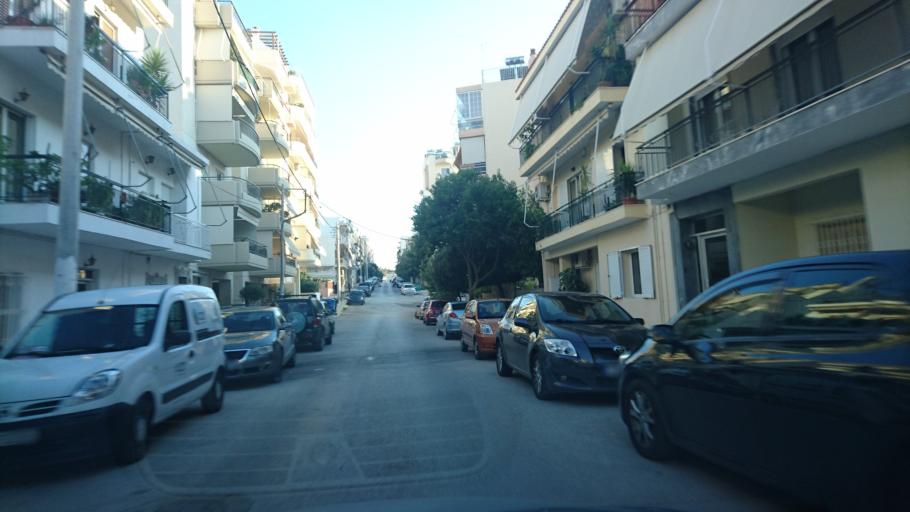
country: GR
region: Attica
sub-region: Nomarchia Athinas
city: Ilioupoli
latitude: 37.9387
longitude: 23.7634
